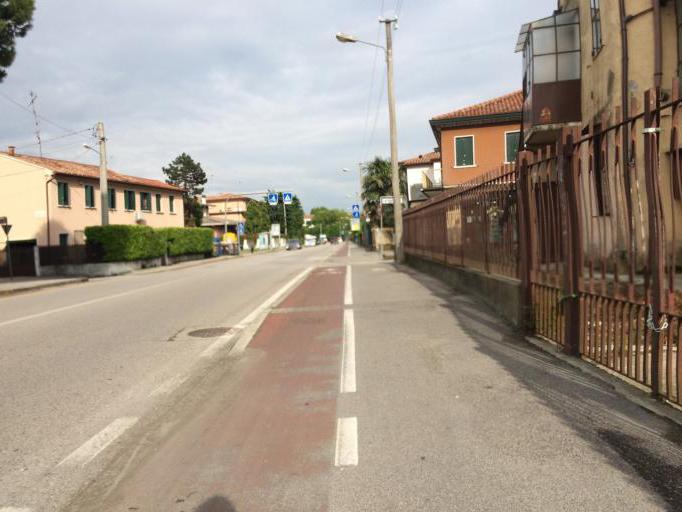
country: IT
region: Veneto
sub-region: Provincia di Padova
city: Padova
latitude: 45.4238
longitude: 11.8895
